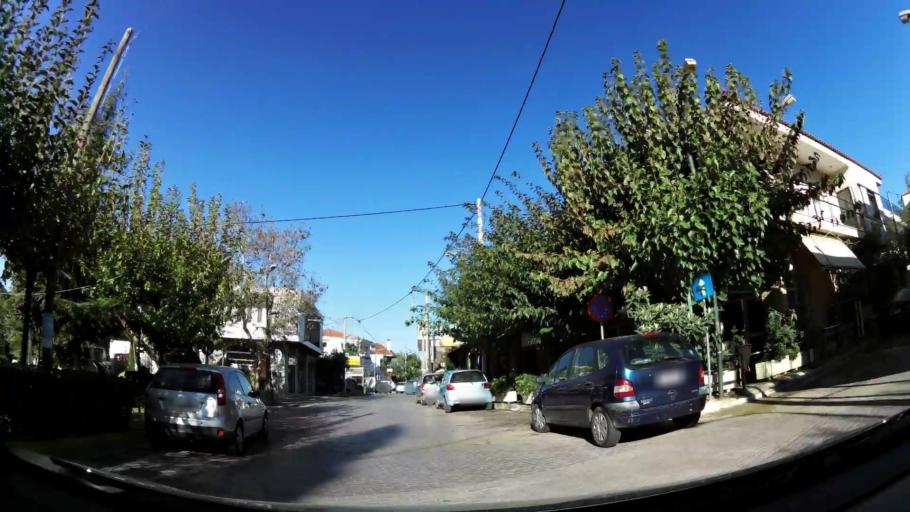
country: GR
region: Attica
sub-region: Nomarchia Anatolikis Attikis
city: Anoixi
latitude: 38.1320
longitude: 23.8609
